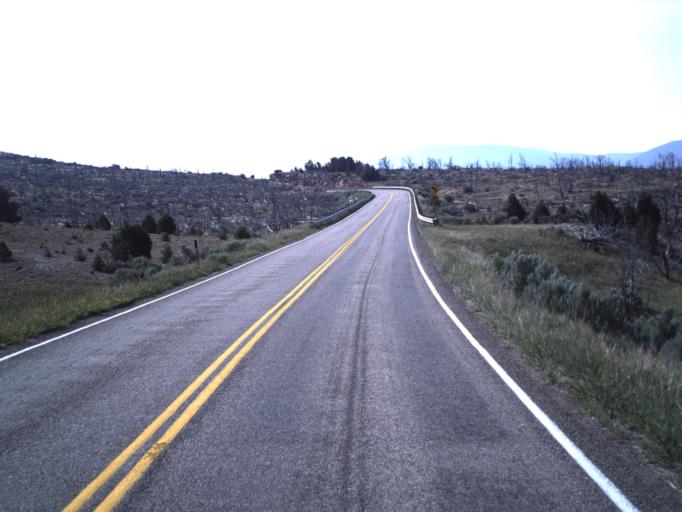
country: US
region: Utah
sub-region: Daggett County
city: Manila
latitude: 40.9441
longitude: -109.4282
